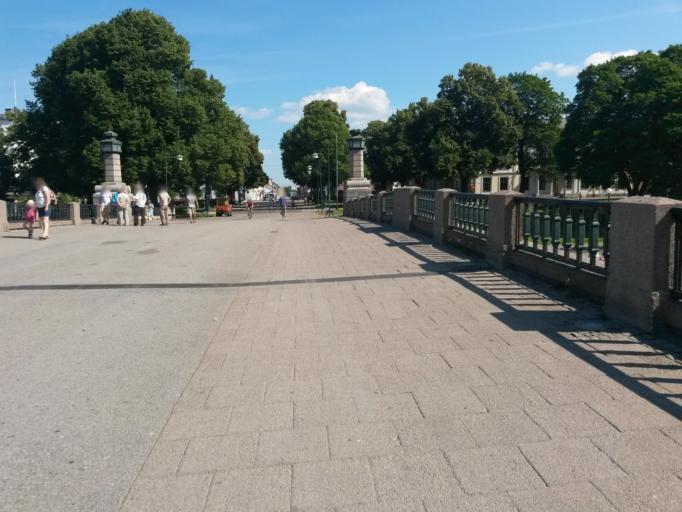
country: SE
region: Vaestra Goetaland
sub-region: Lidkopings Kommun
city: Lidkoping
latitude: 58.5033
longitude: 13.1594
